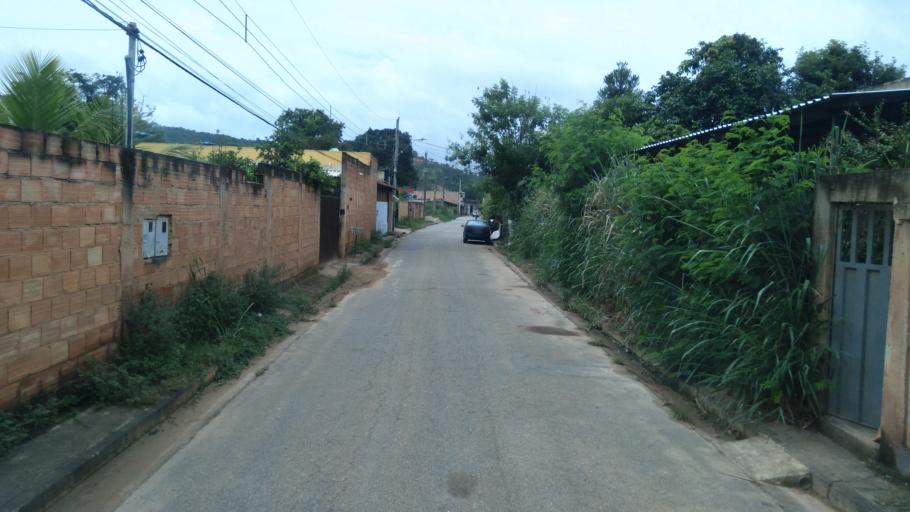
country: BR
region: Minas Gerais
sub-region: Santa Luzia
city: Santa Luzia
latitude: -19.8366
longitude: -43.8649
